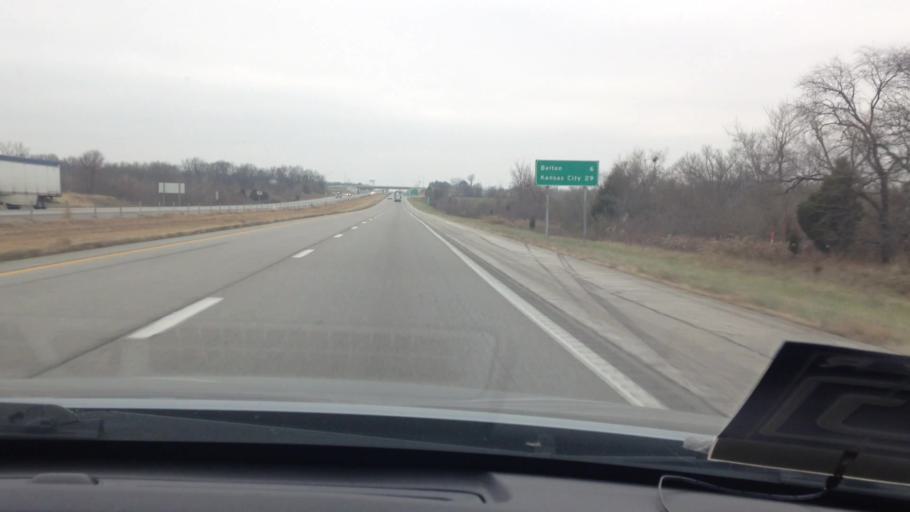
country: US
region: Missouri
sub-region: Cass County
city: Peculiar
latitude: 38.7326
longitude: -94.4638
